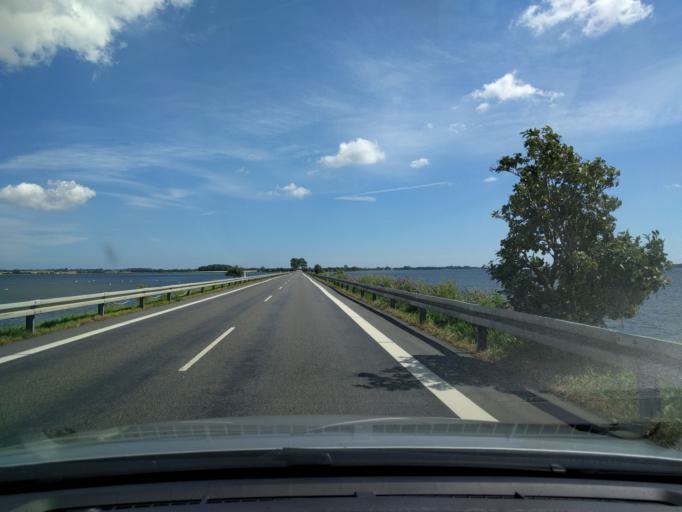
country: DK
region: Zealand
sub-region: Guldborgsund Kommune
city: Stubbekobing
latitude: 54.9080
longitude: 12.0856
